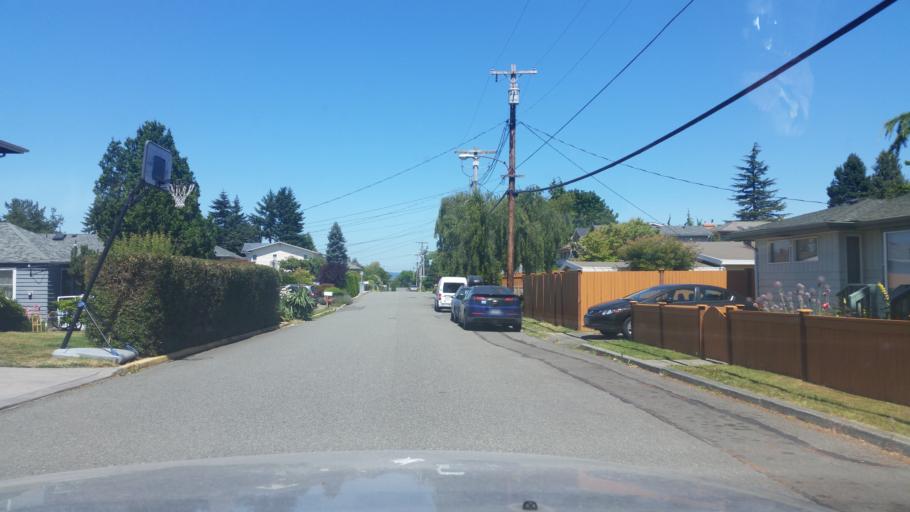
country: US
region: Washington
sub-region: Snohomish County
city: Edmonds
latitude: 47.8048
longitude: -122.3742
